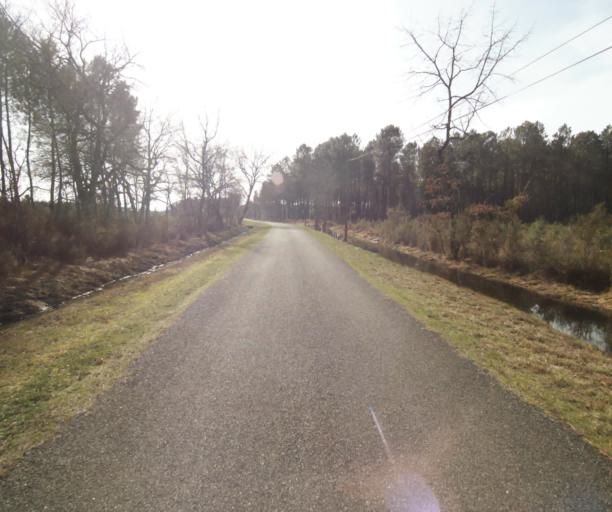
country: FR
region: Aquitaine
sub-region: Departement des Landes
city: Roquefort
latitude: 44.1355
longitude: -0.1863
